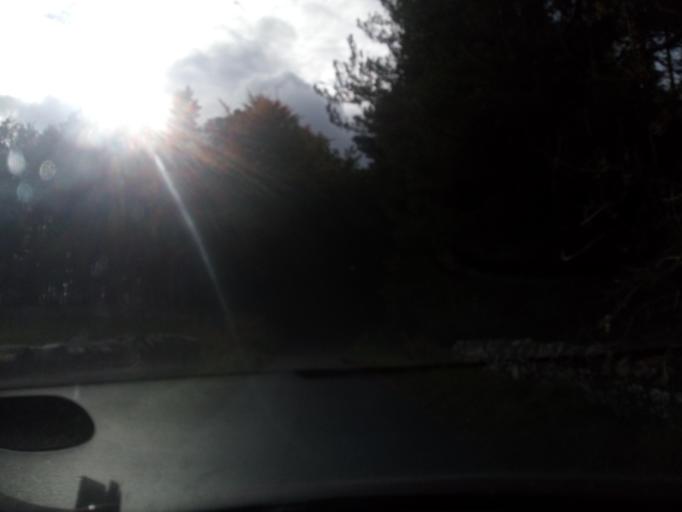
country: GB
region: Scotland
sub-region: The Scottish Borders
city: Galashiels
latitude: 55.6694
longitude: -2.7976
